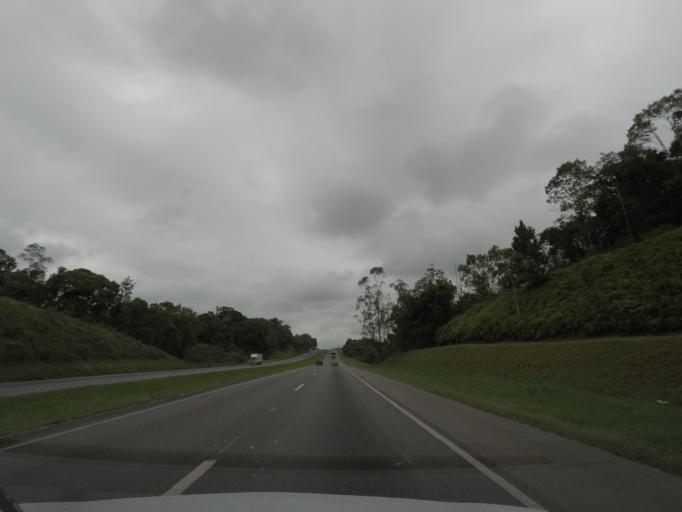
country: BR
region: Sao Paulo
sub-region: Registro
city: Registro
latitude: -24.4484
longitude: -47.8061
